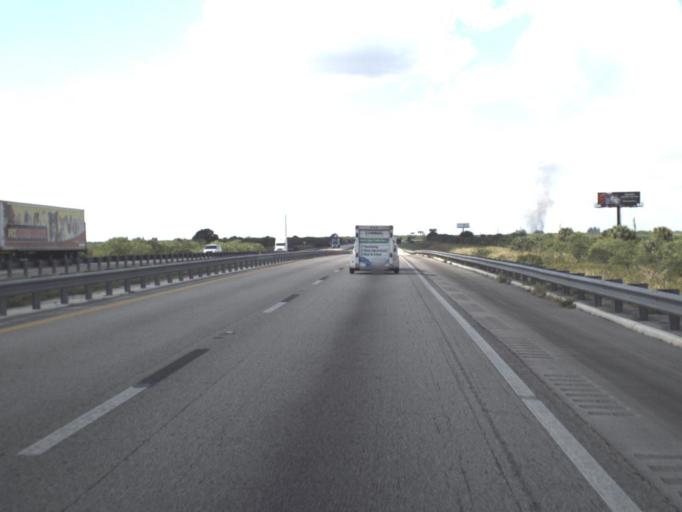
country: US
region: Florida
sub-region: Saint Lucie County
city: Lakewood Park
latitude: 27.4847
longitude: -80.4811
